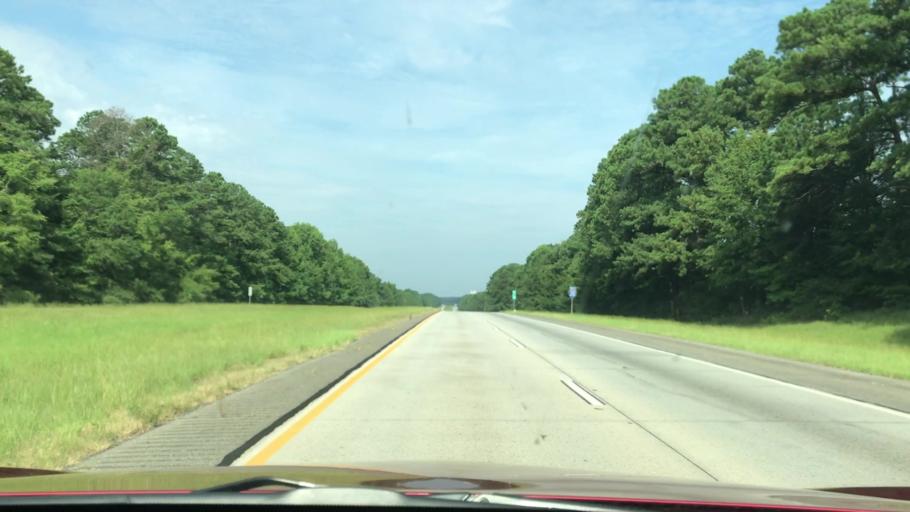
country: US
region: Georgia
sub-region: Warren County
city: Firing Range
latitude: 33.5035
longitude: -82.7221
